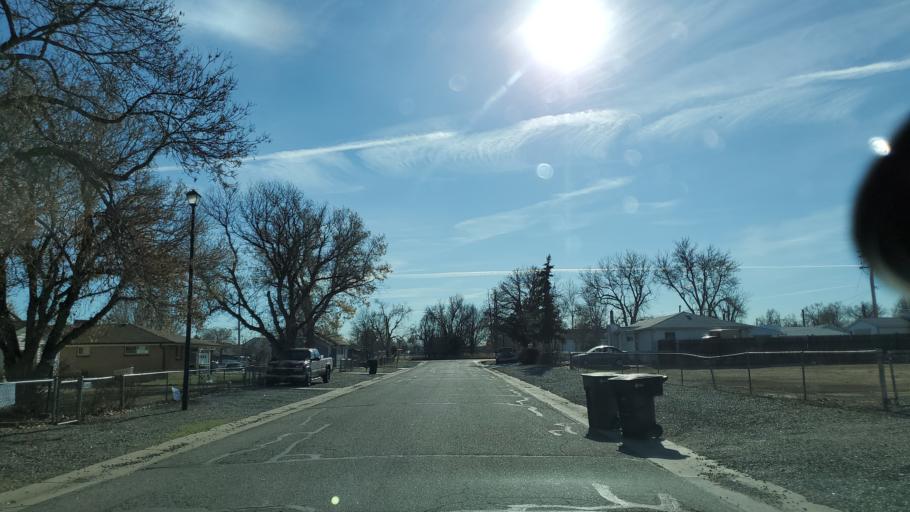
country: US
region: Colorado
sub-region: Adams County
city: Northglenn
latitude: 39.9222
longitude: -104.9599
